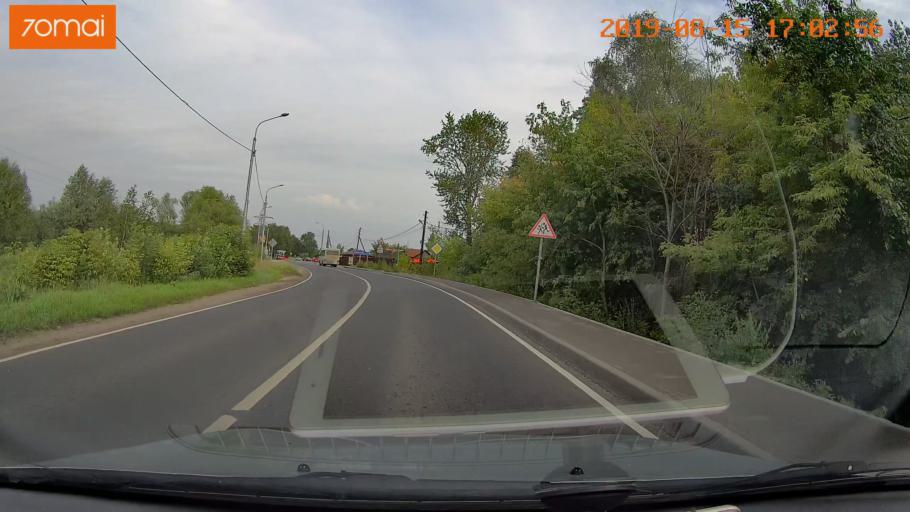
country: RU
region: Moskovskaya
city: Malyshevo
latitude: 55.4829
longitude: 38.3981
